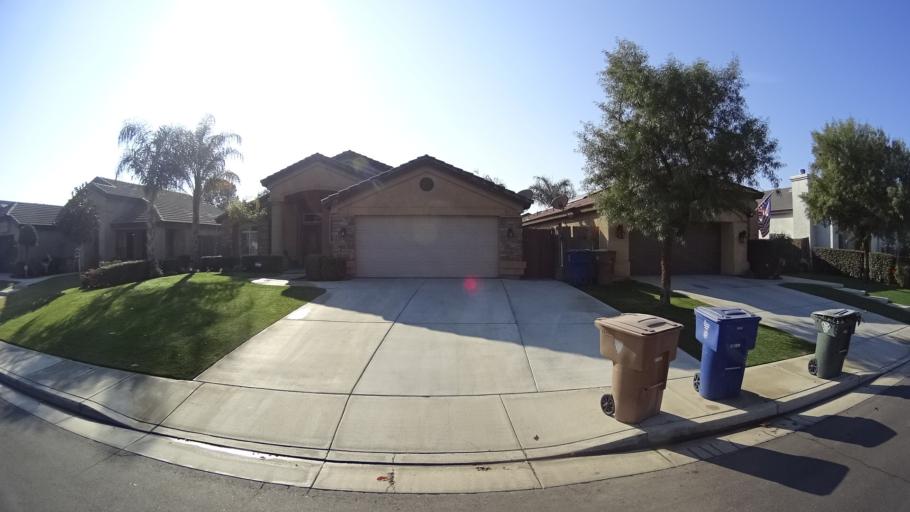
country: US
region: California
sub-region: Kern County
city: Greenacres
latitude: 35.3082
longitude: -119.1177
